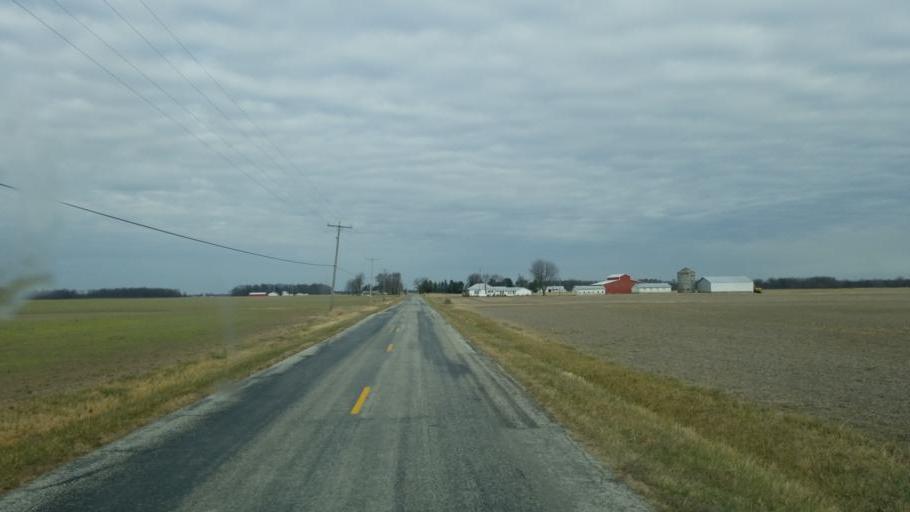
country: US
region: Ohio
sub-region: Hardin County
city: Forest
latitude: 40.6566
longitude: -83.4196
